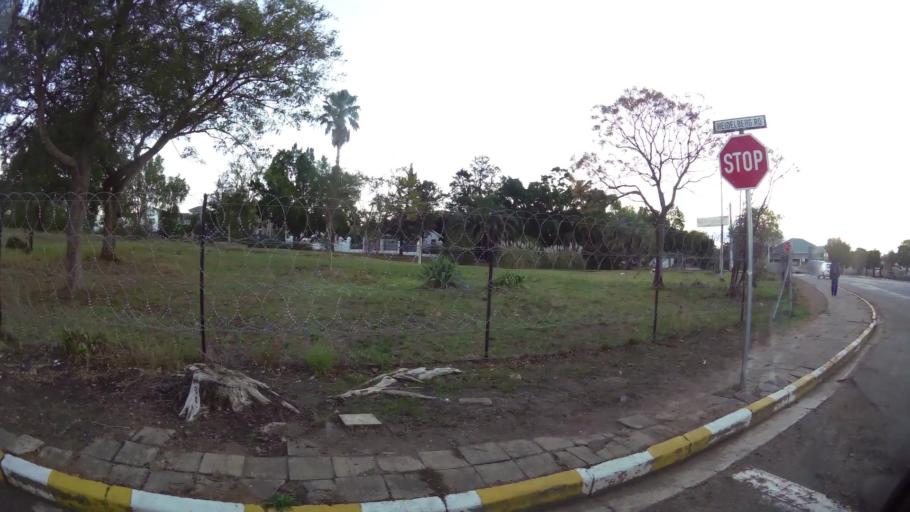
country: ZA
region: Western Cape
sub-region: Eden District Municipality
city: Riversdale
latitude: -34.0918
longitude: 21.2558
